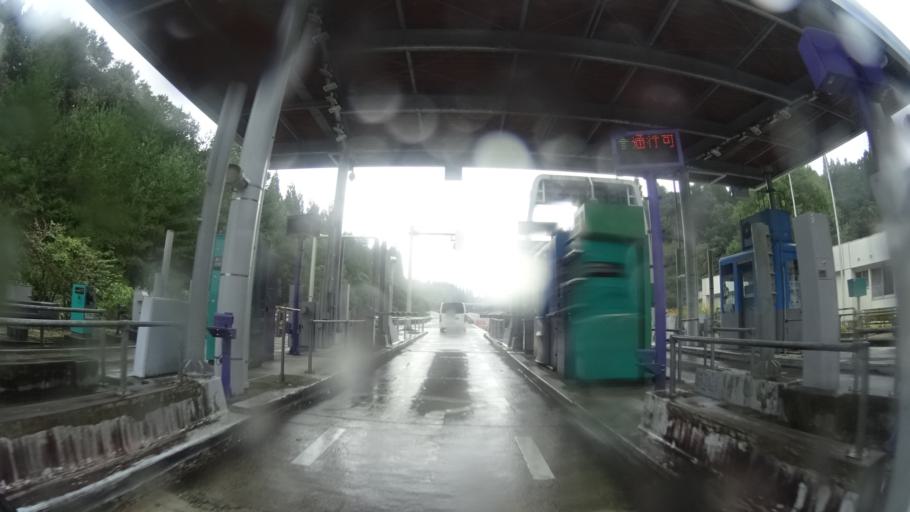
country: JP
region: Kagoshima
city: Kajiki
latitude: 31.9002
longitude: 130.7030
